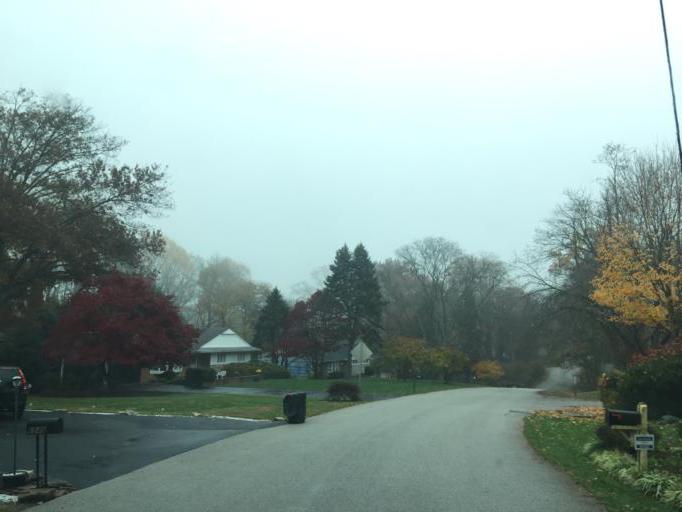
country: US
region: Maryland
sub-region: Howard County
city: Riverside
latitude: 39.1913
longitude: -76.8555
